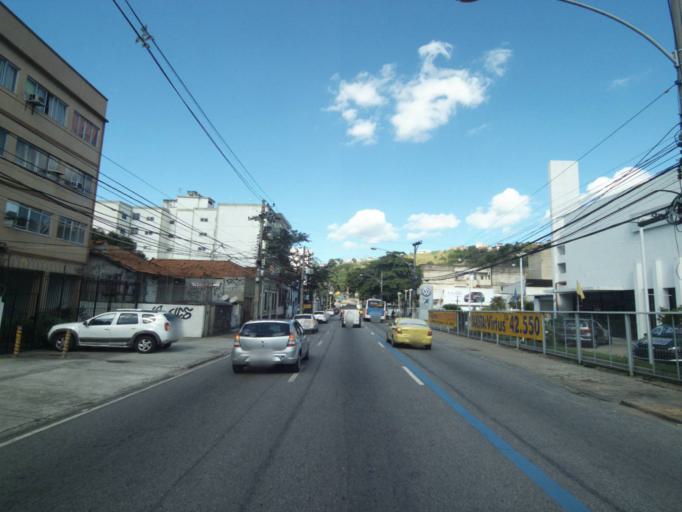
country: BR
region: Rio de Janeiro
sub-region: Rio De Janeiro
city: Rio de Janeiro
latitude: -22.9040
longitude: -43.2450
